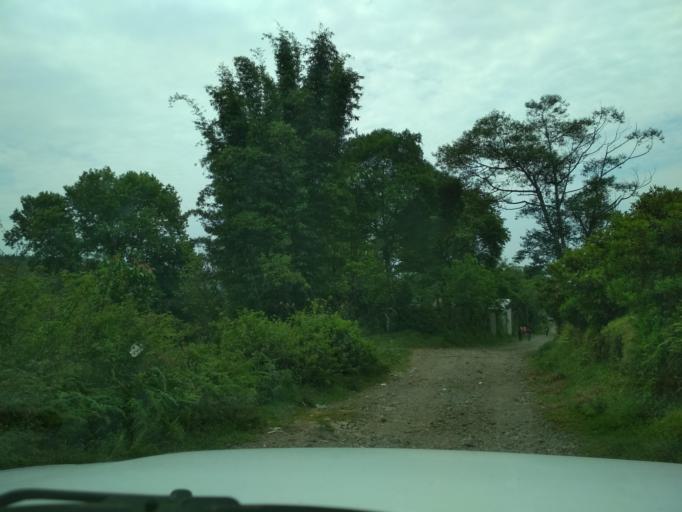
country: MX
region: Veracruz
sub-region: La Perla
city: La Perla
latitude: 18.9256
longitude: -97.1278
